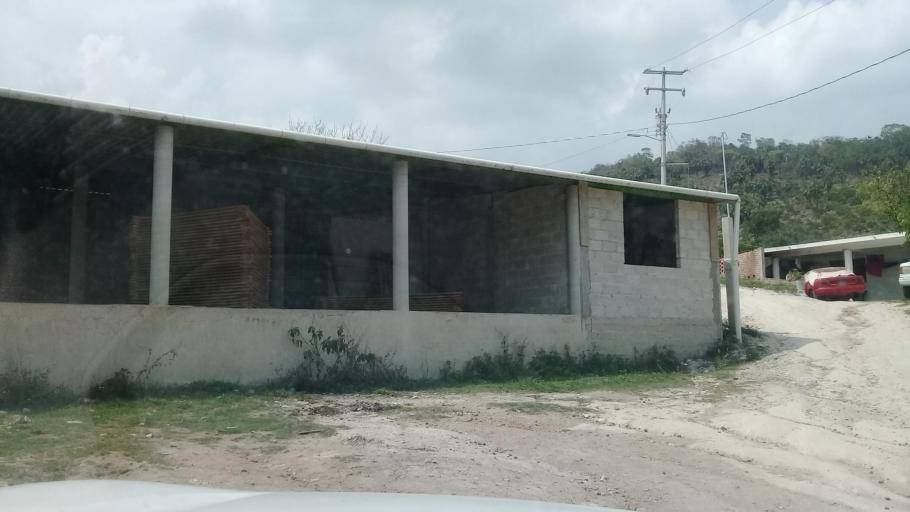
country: MX
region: Veracruz
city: Jalcomulco
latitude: 19.3972
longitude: -96.7878
